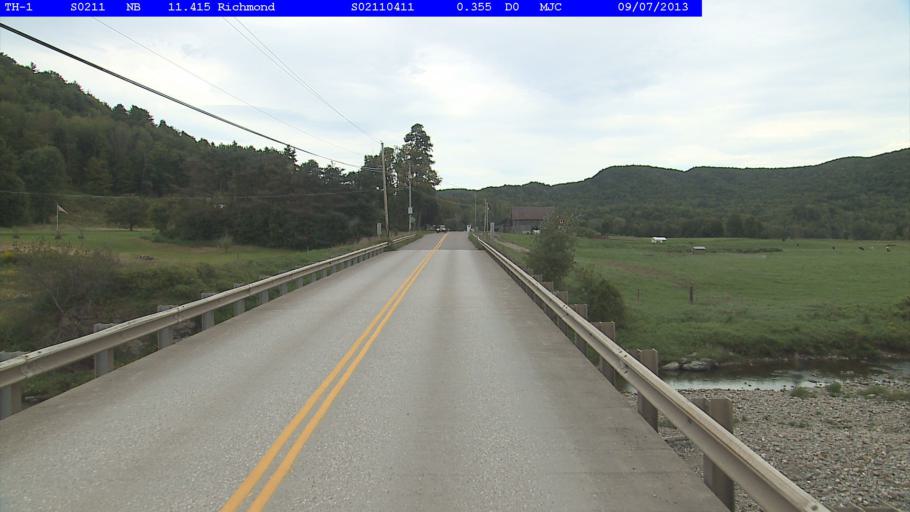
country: US
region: Vermont
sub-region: Chittenden County
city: Williston
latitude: 44.3583
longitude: -72.9930
